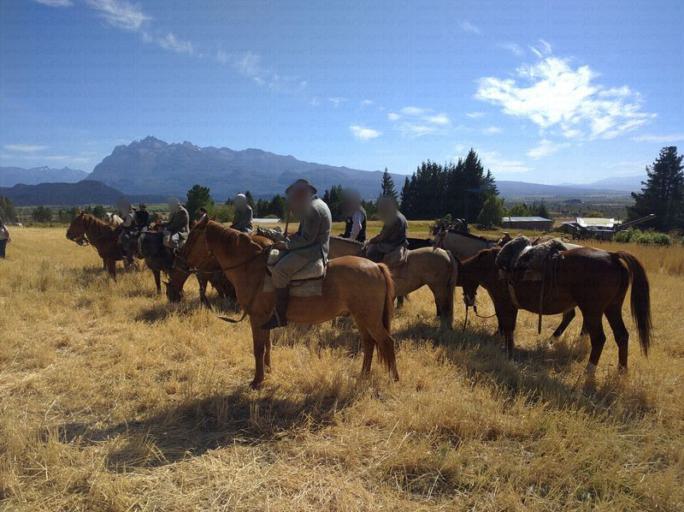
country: AR
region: Chubut
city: Trevelin
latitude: -43.2039
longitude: -71.5620
